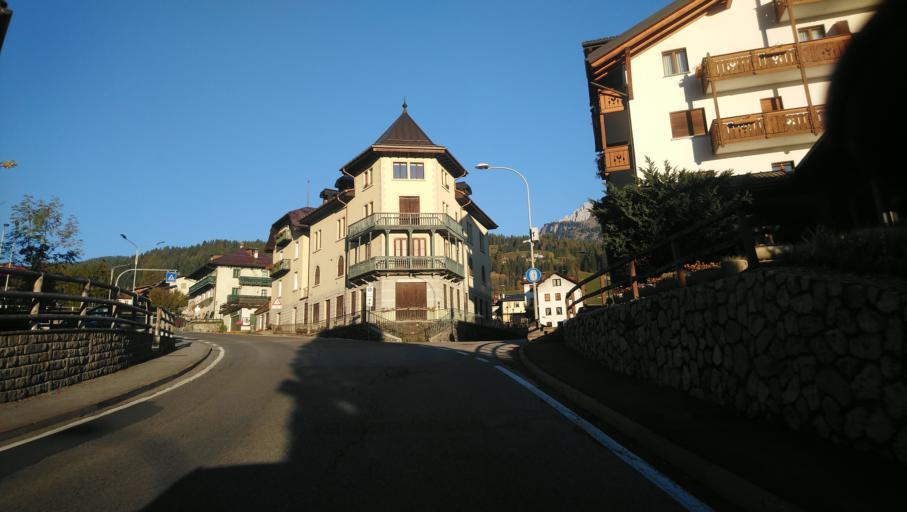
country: IT
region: Veneto
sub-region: Provincia di Belluno
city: Canale d'Agordo
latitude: 46.3636
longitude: 11.8992
